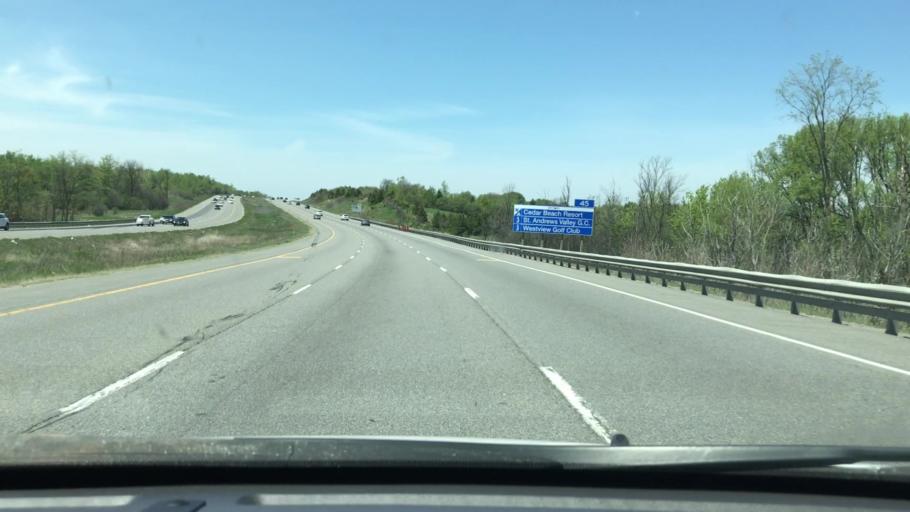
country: CA
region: Ontario
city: Newmarket
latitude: 43.9983
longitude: -79.3974
